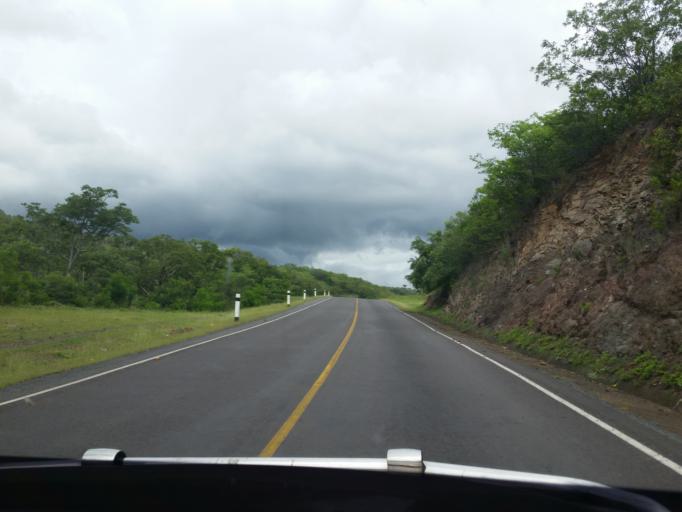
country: NI
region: Matagalpa
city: Matagalpa
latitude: 12.9344
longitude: -86.0140
